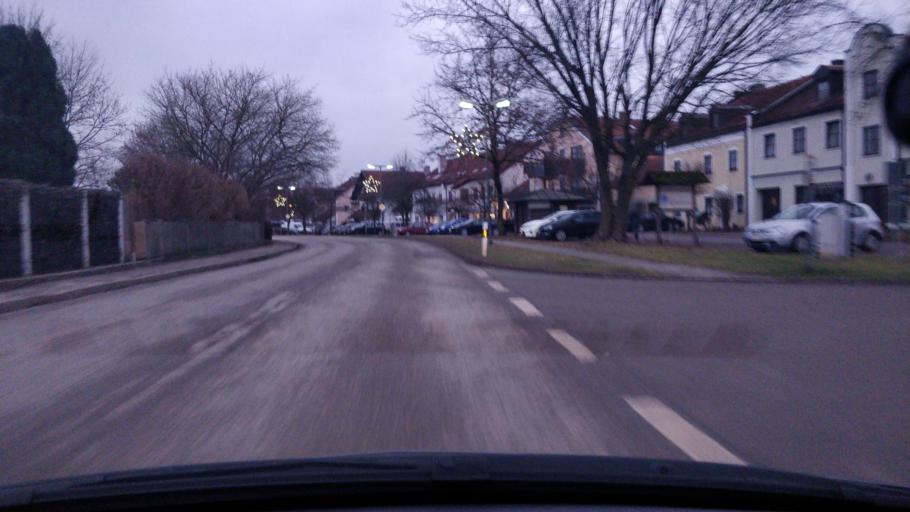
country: DE
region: Bavaria
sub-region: Upper Bavaria
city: Schwindegg
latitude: 48.2720
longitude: 12.2633
